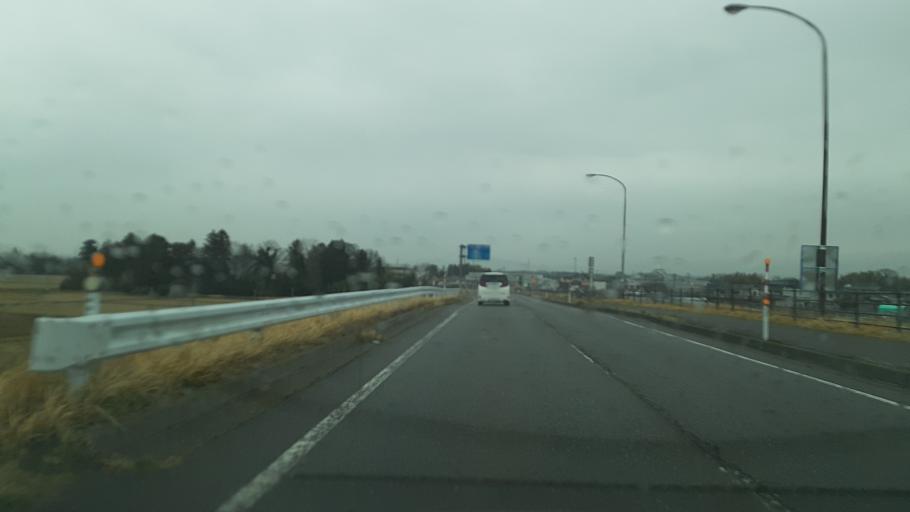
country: JP
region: Niigata
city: Kameda-honcho
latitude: 37.8814
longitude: 139.1691
